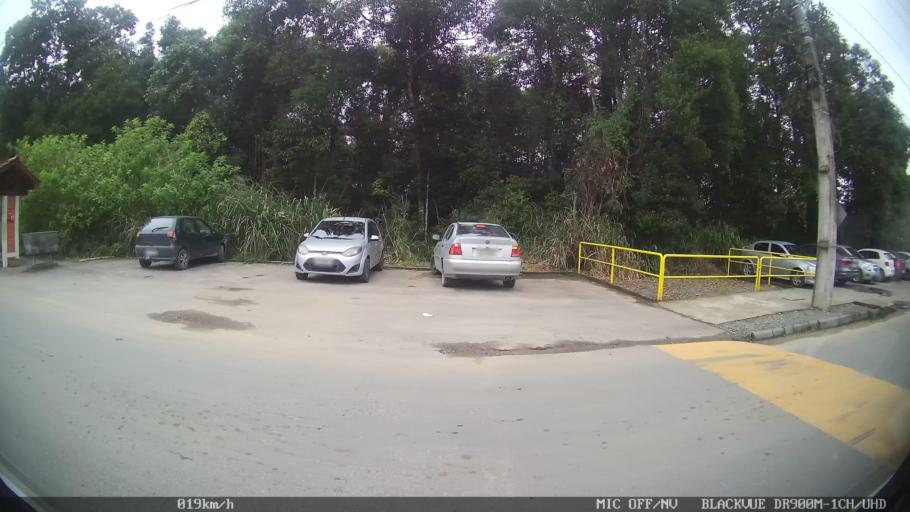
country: BR
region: Santa Catarina
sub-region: Joinville
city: Joinville
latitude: -26.2780
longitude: -48.9164
